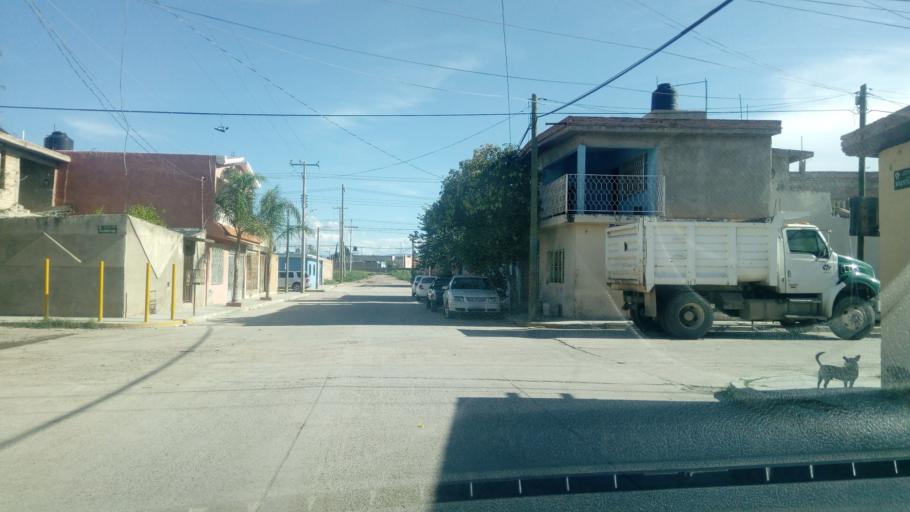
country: MX
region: Durango
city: Victoria de Durango
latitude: 24.0072
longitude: -104.6294
